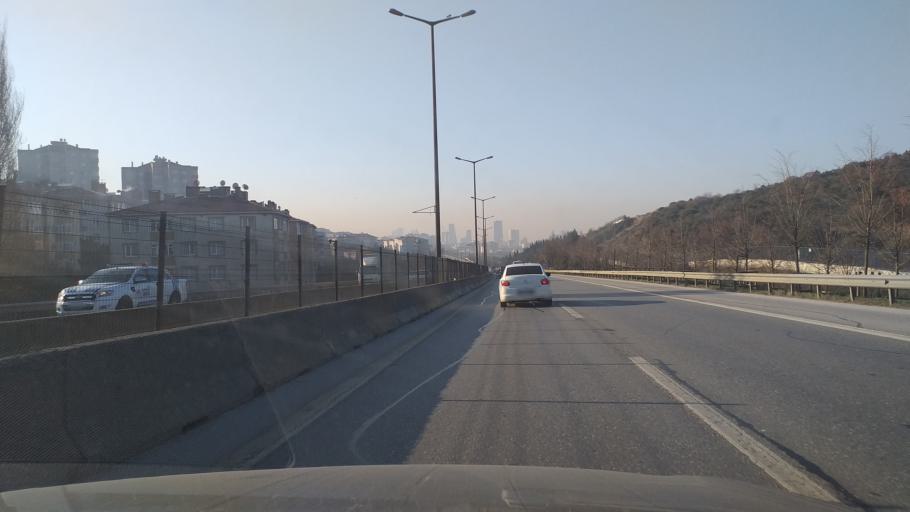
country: TR
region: Istanbul
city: Maltepe
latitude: 40.9357
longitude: 29.2086
